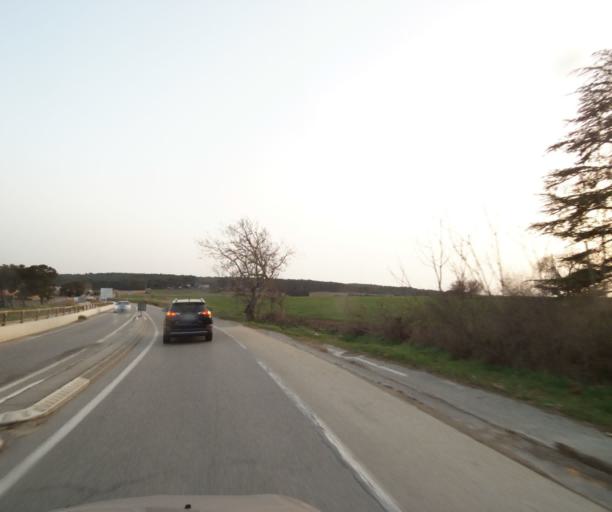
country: FR
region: Provence-Alpes-Cote d'Azur
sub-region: Departement des Bouches-du-Rhone
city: Cabries
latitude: 43.4451
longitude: 5.3605
